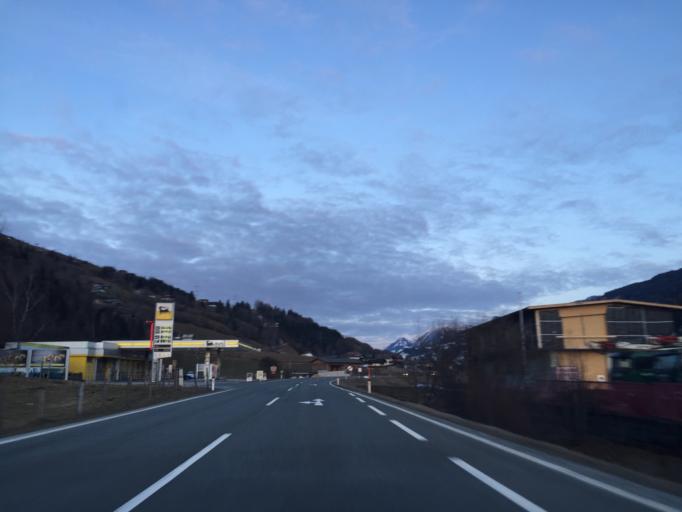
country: AT
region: Salzburg
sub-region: Politischer Bezirk Zell am See
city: Taxenbach
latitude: 47.2891
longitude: 12.9040
